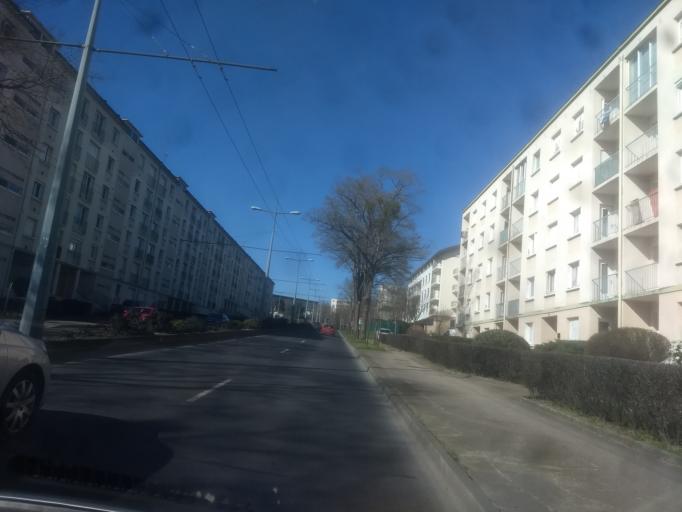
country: FR
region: Limousin
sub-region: Departement de la Haute-Vienne
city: Limoges
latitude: 45.8202
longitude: 1.2484
